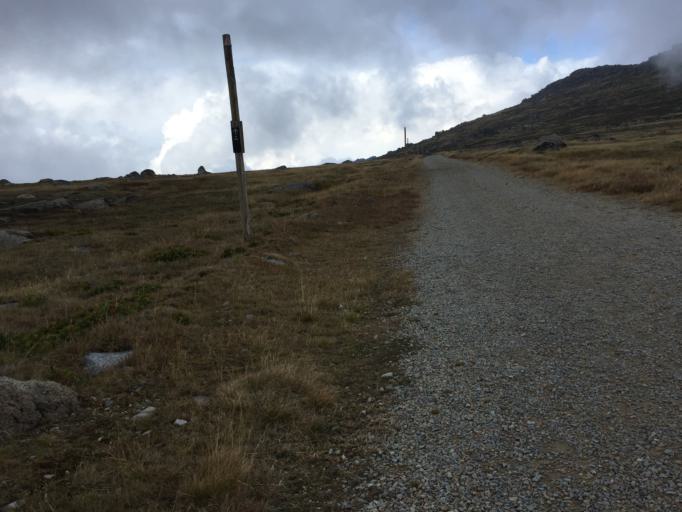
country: AU
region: New South Wales
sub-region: Snowy River
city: Jindabyne
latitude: -36.4578
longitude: 148.2984
